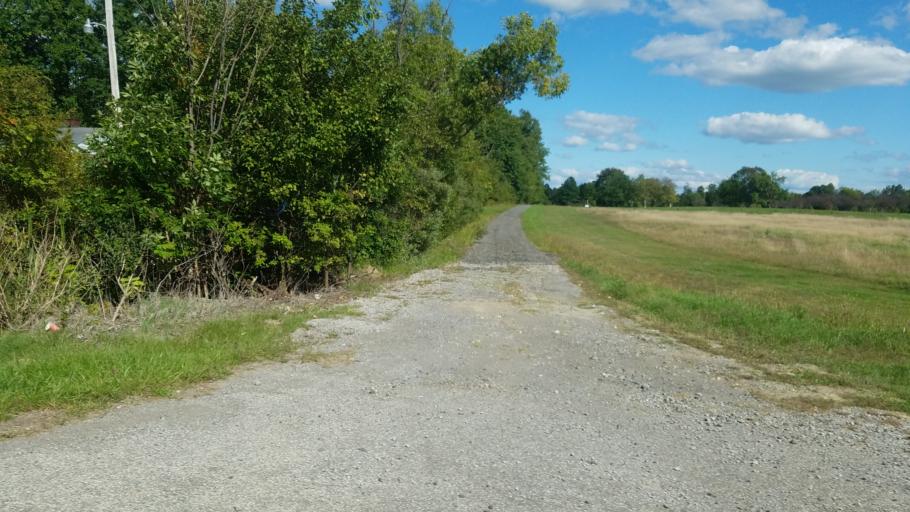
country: US
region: Ohio
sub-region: Mahoning County
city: Austintown
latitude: 41.0650
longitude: -80.7606
